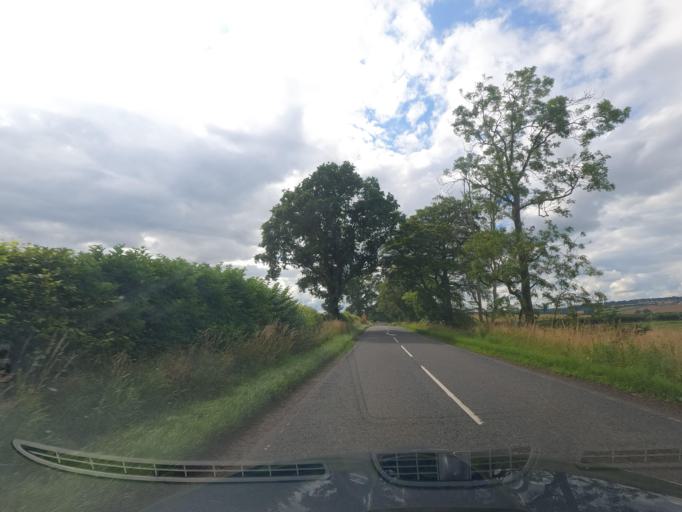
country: GB
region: Scotland
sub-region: The Scottish Borders
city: Kelso
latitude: 55.7031
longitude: -2.4333
